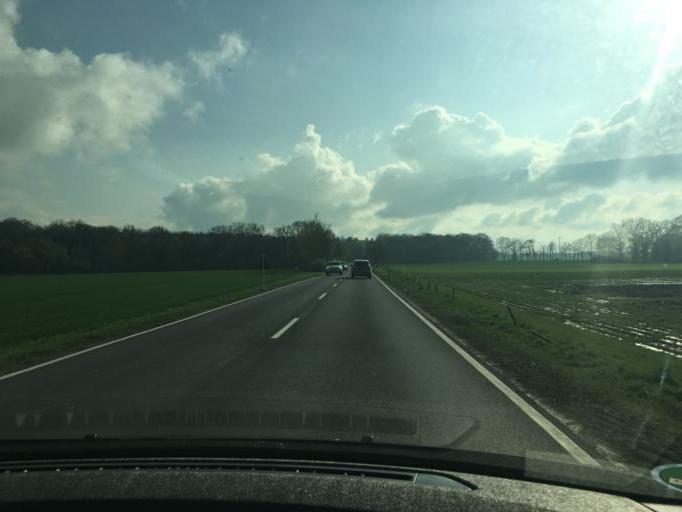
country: DE
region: North Rhine-Westphalia
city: Bornheim
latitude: 50.7294
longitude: 6.9354
